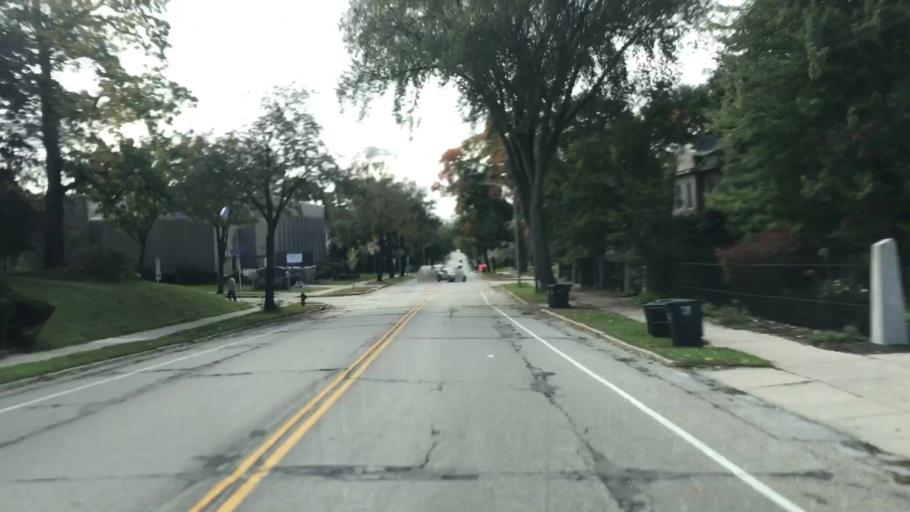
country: US
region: Wisconsin
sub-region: Milwaukee County
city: Wauwatosa
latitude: 43.0594
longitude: -88.0075
